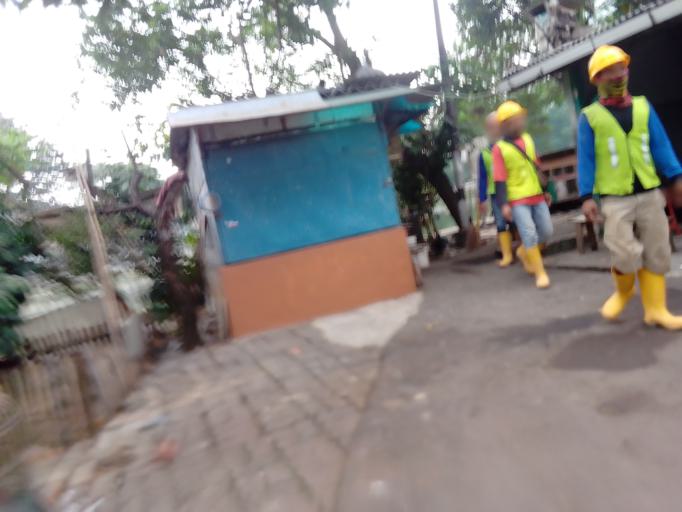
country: ID
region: Jakarta Raya
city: Jakarta
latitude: -6.2004
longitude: 106.8185
